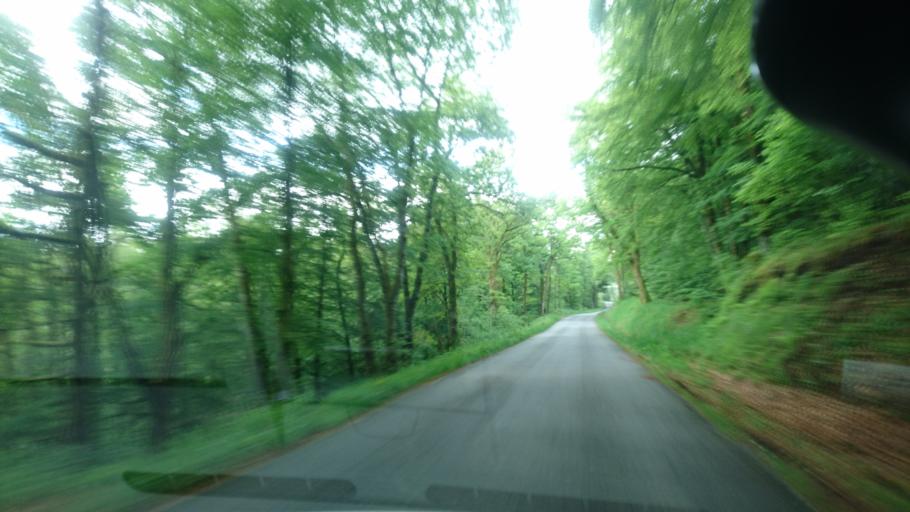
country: FR
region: Limousin
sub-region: Departement de la Haute-Vienne
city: Peyrat-le-Chateau
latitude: 45.7913
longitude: 1.9181
